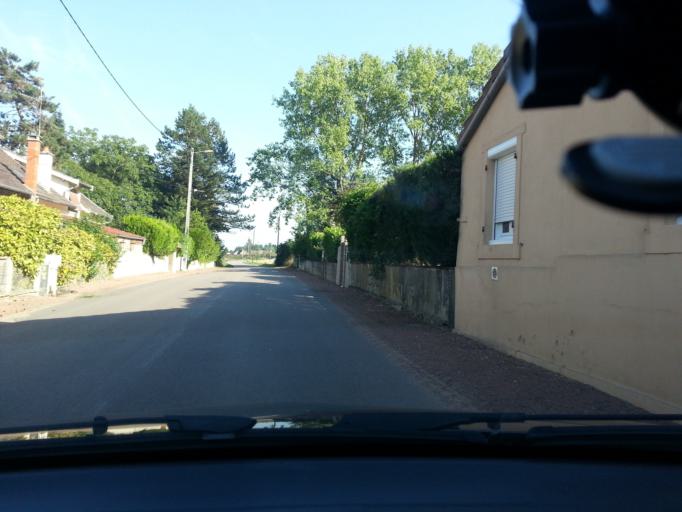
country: FR
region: Bourgogne
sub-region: Departement de Saone-et-Loire
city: Saint-Remy
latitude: 46.7594
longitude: 4.8120
